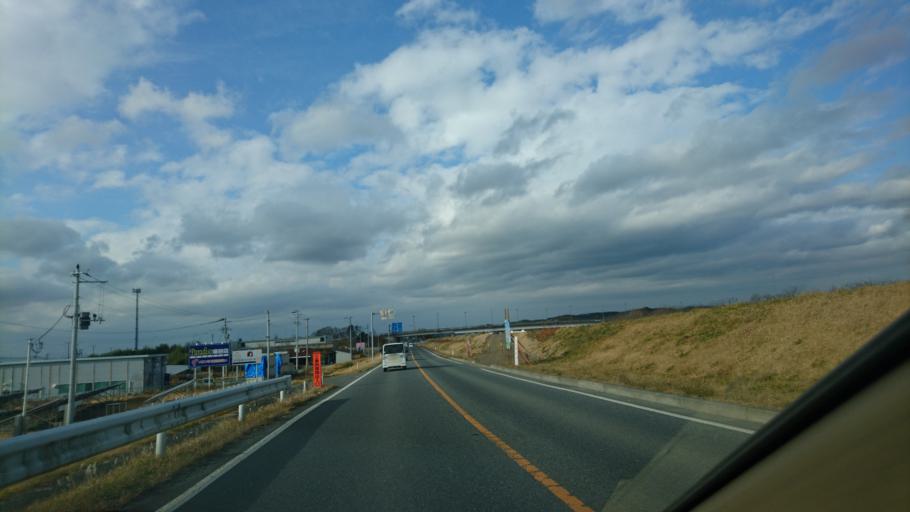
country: JP
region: Miyagi
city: Wakuya
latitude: 38.5301
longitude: 141.1448
